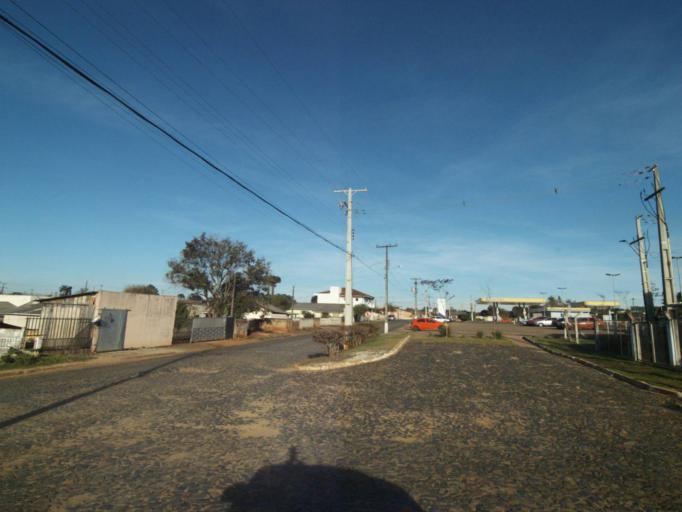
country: BR
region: Parana
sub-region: Tibagi
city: Tibagi
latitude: -24.5088
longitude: -50.4170
